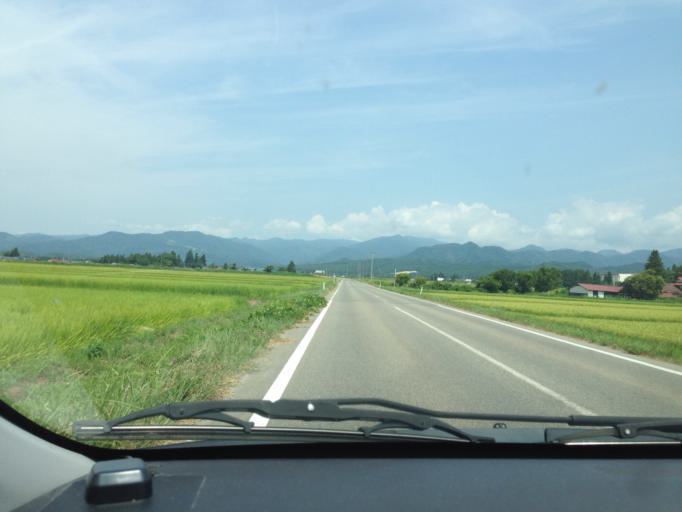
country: JP
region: Fukushima
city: Kitakata
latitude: 37.6656
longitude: 139.8812
